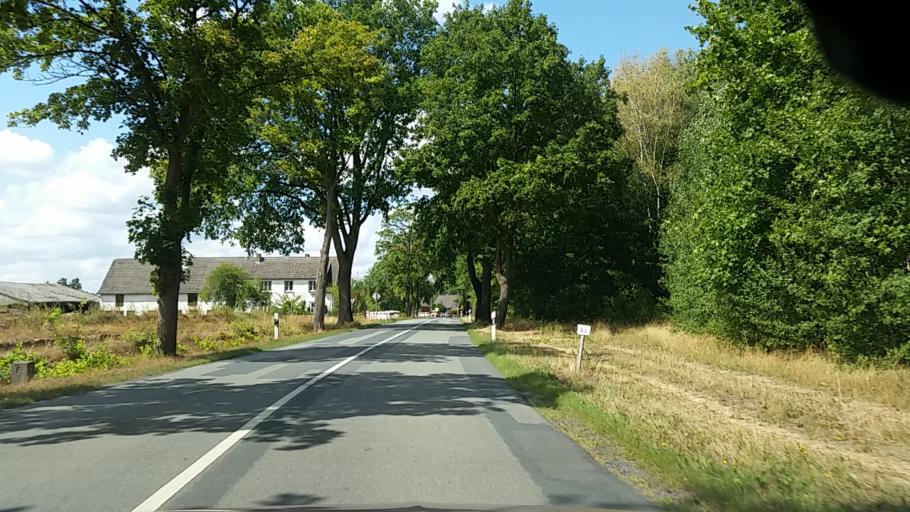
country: DE
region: Lower Saxony
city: Hankensbuttel
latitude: 52.7087
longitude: 10.6285
